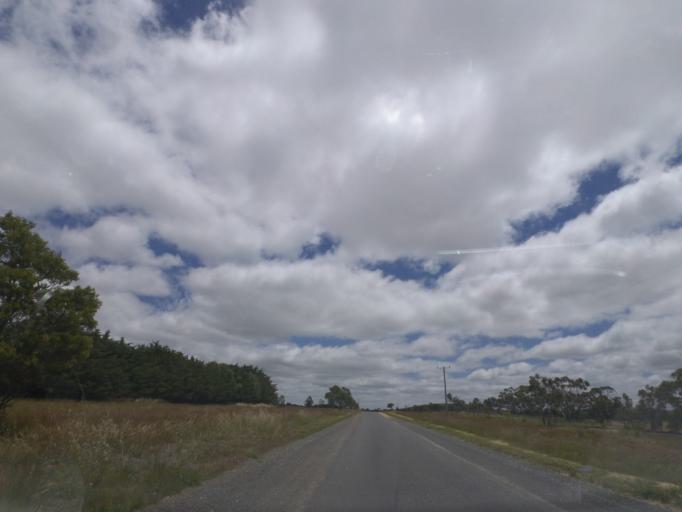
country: AU
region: Victoria
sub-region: Moorabool
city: Bacchus Marsh
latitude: -37.6248
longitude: 144.2610
